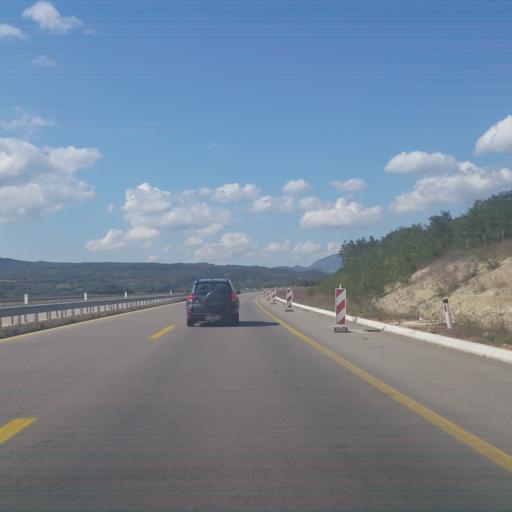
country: RS
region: Central Serbia
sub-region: Pirotski Okrug
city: Bela Palanka
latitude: 43.2390
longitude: 22.2894
